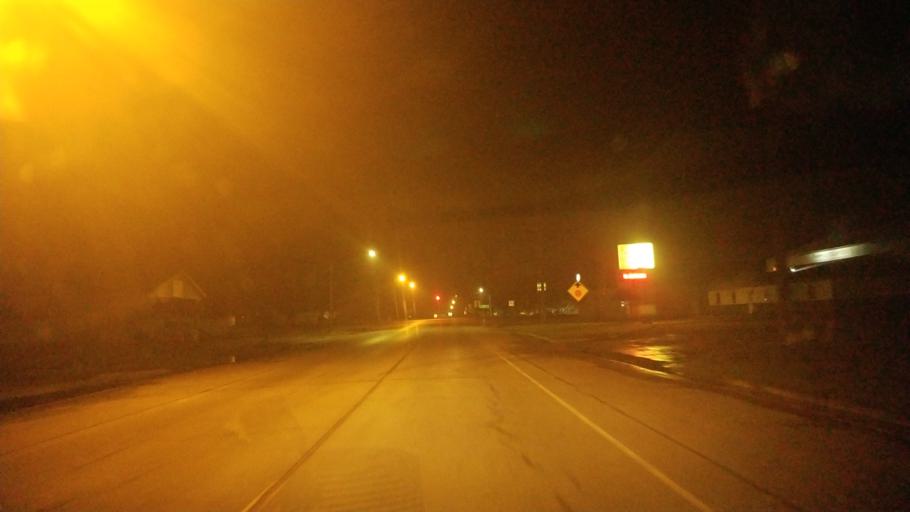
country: US
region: Missouri
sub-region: Pike County
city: Bowling Green
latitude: 39.3478
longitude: -91.2061
